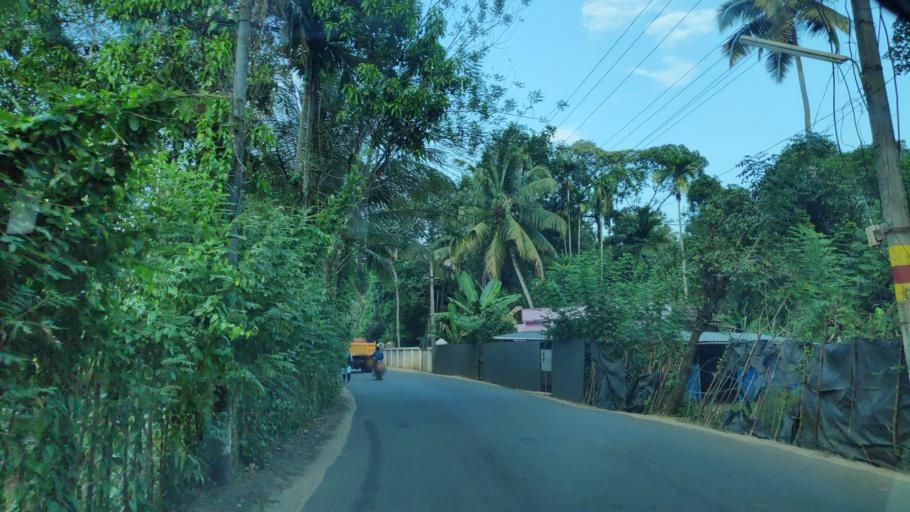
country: IN
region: Kerala
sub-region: Alappuzha
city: Shertallai
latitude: 9.6694
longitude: 76.3885
